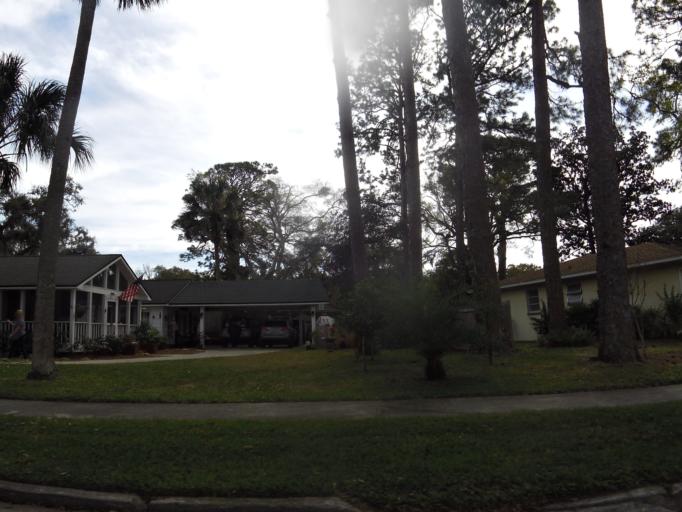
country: US
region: Florida
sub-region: Saint Johns County
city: Saint Augustine
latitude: 29.9170
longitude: -81.3178
